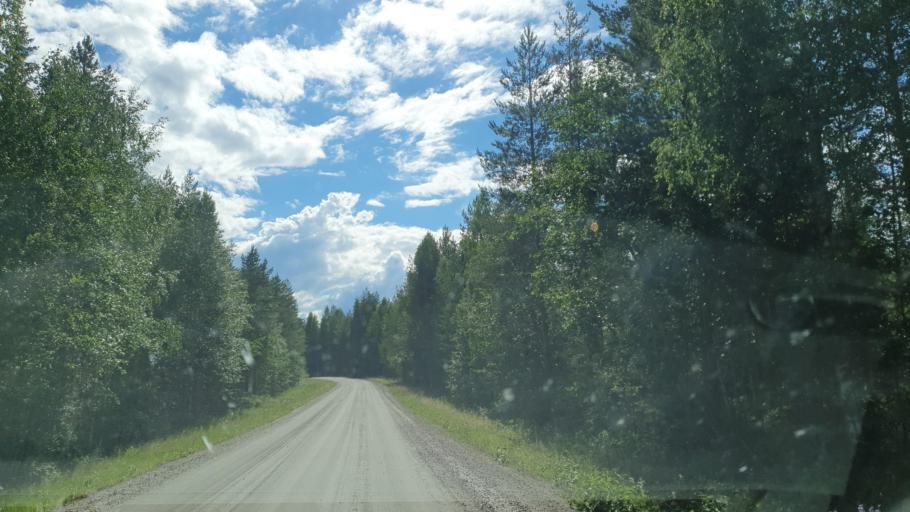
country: FI
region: Kainuu
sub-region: Kehys-Kainuu
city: Kuhmo
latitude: 64.1440
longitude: 29.7054
